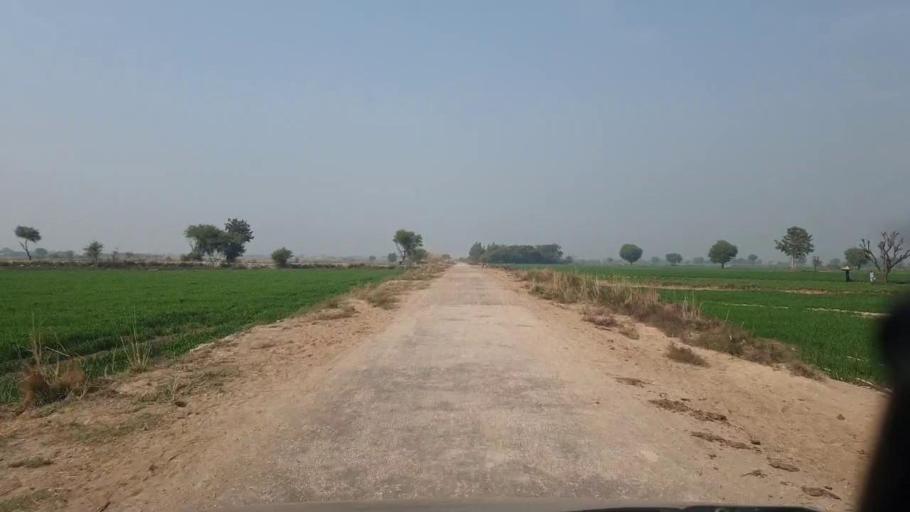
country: PK
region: Sindh
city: Shahdadpur
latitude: 26.0280
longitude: 68.5307
